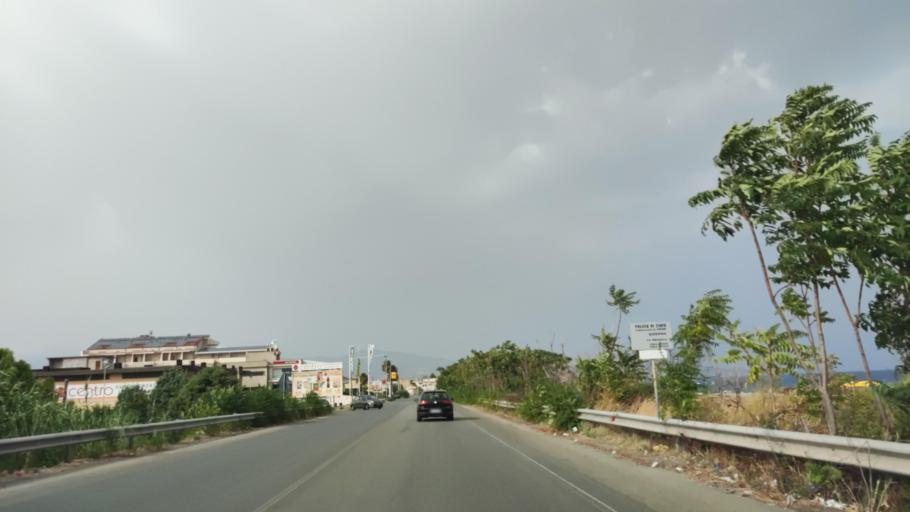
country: IT
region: Calabria
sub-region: Provincia di Reggio Calabria
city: Siderno
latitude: 38.2529
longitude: 16.2815
